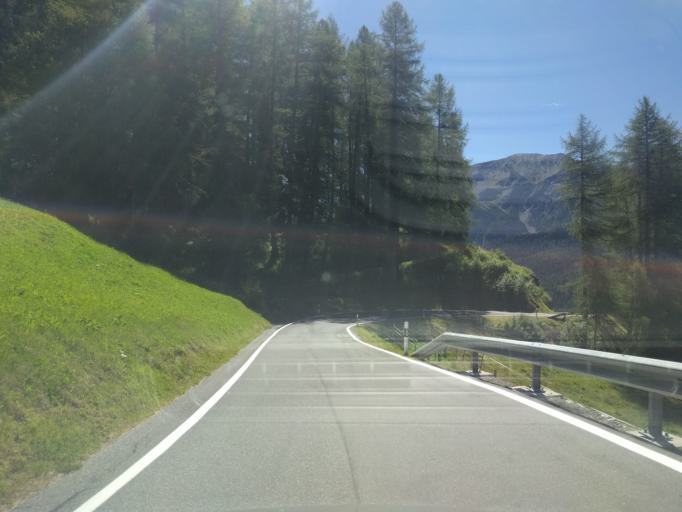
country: IT
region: Trentino-Alto Adige
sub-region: Bolzano
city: Tubre
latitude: 46.6158
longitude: 10.3770
